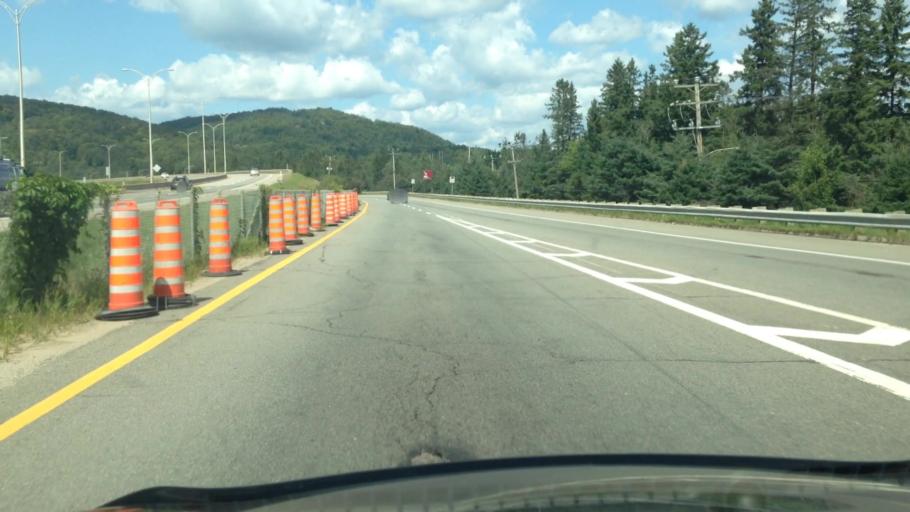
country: CA
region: Quebec
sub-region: Laurentides
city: Mont-Tremblant
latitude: 46.1288
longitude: -74.6099
